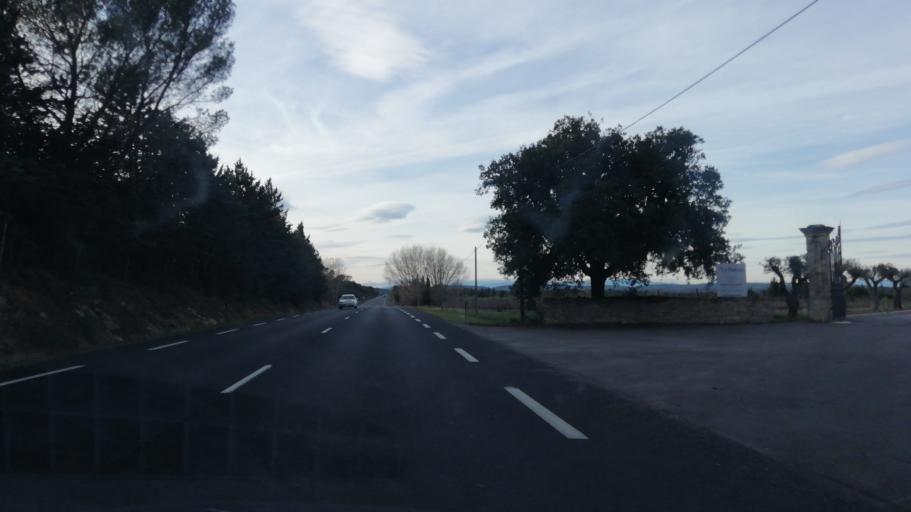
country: FR
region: Languedoc-Roussillon
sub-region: Departement du Gard
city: Clarensac
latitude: 43.8567
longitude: 4.2416
